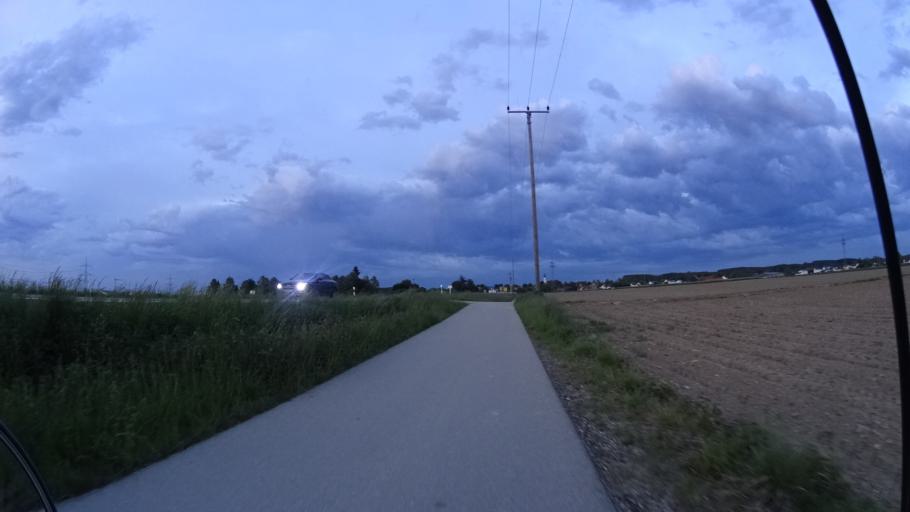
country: DE
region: Bavaria
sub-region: Swabia
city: Pfaffenhofen an der Roth
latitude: 48.3534
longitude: 10.1456
